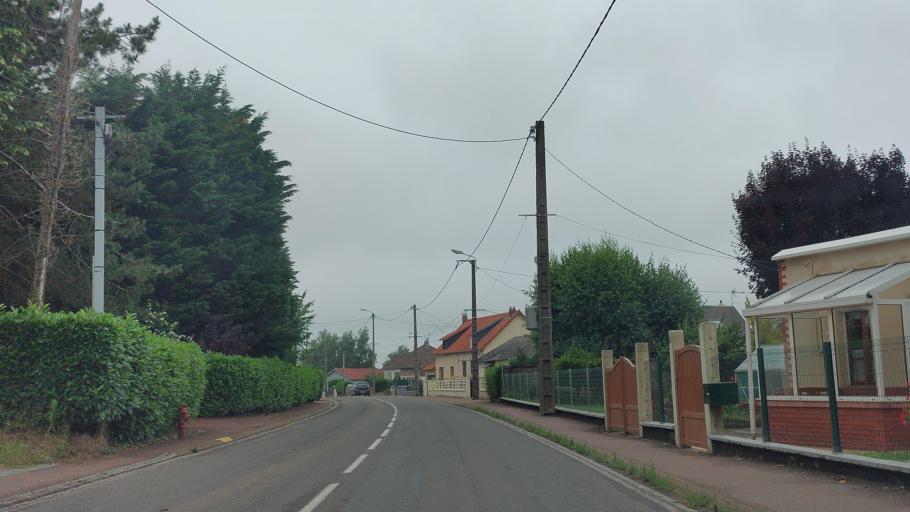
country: FR
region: Picardie
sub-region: Departement de la Somme
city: Bethencourt-sur-Mer
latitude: 50.0812
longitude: 1.4981
